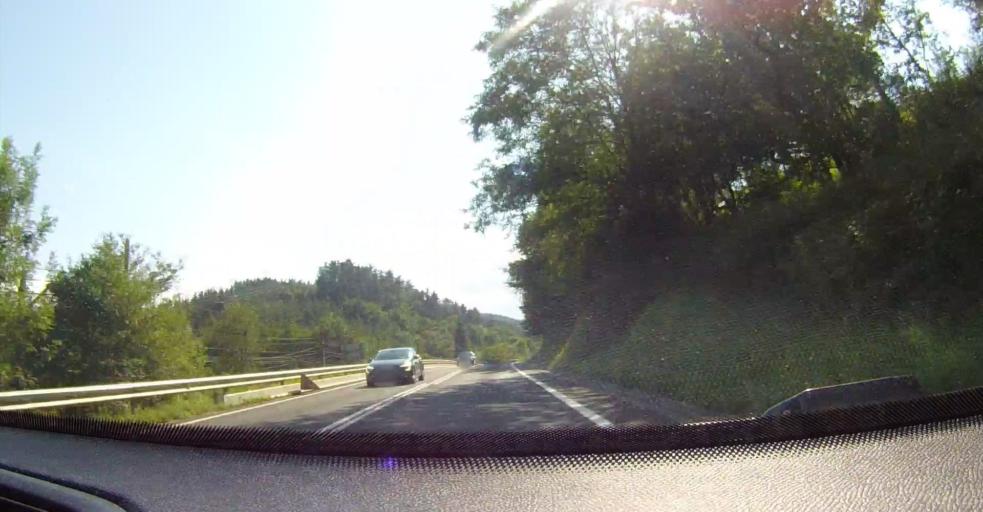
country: ES
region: Basque Country
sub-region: Bizkaia
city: Muxika
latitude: 43.2502
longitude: -2.6967
